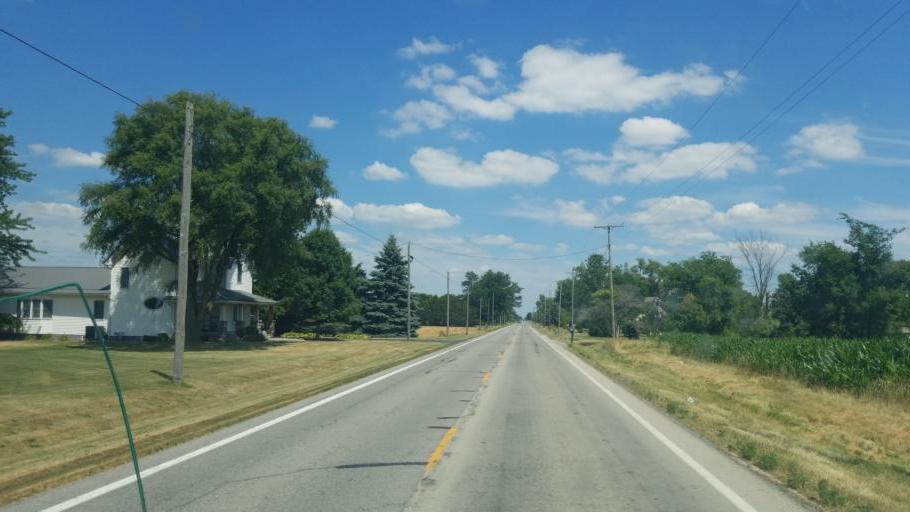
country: US
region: Ohio
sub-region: Defiance County
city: Hicksville
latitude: 41.2959
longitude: -84.7434
